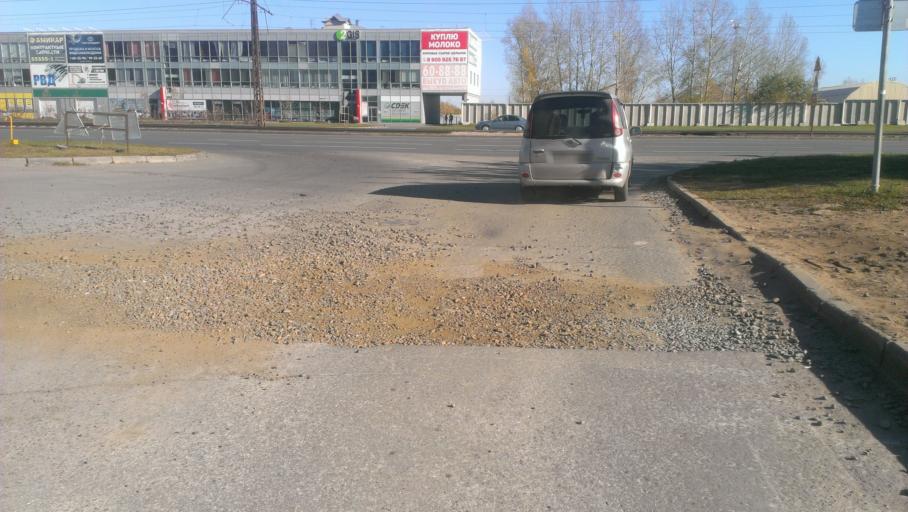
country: RU
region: Altai Krai
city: Novosilikatnyy
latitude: 53.3291
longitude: 83.6918
